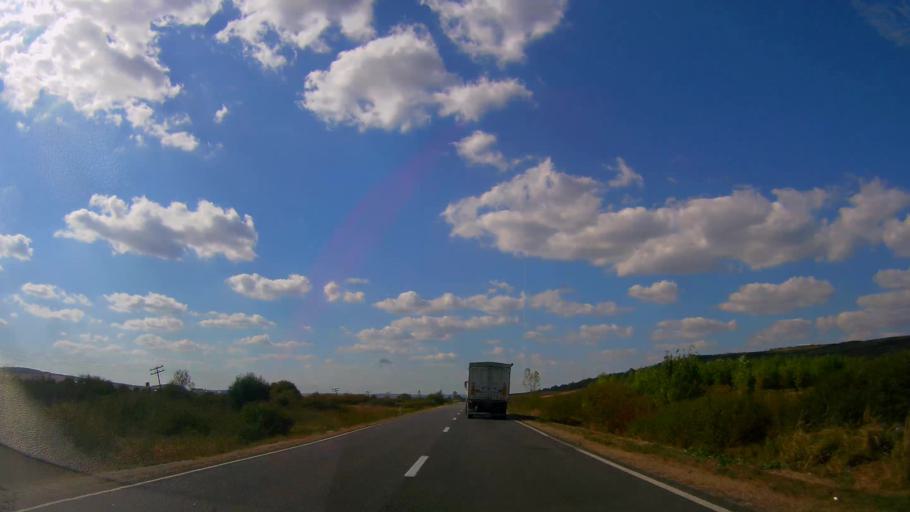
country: RO
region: Salaj
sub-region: Comuna Bocsa
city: Bocsa
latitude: 47.3252
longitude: 22.8785
